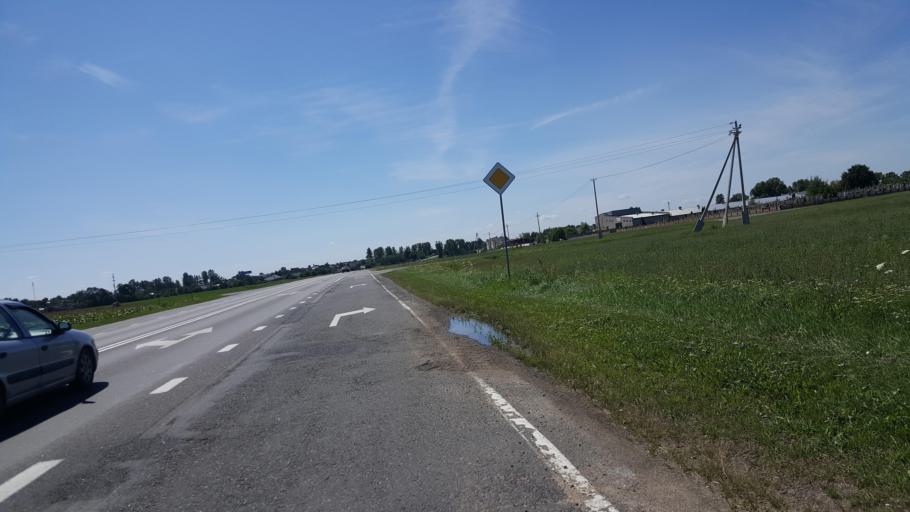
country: BY
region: Brest
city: Charnawchytsy
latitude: 52.2214
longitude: 23.7495
